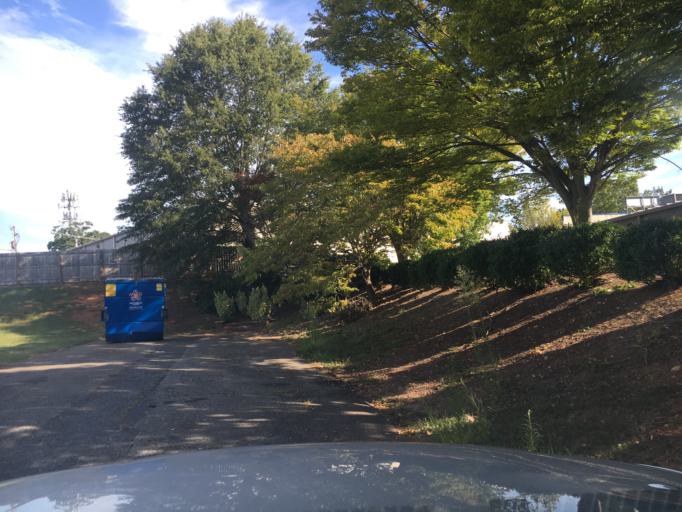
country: US
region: North Carolina
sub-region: Catawba County
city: Hickory
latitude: 35.7486
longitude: -81.3368
